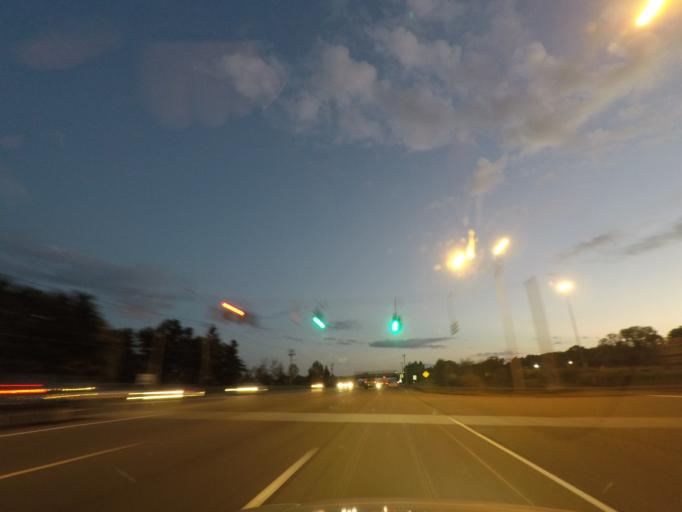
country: US
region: New York
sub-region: Orange County
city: Gardnertown
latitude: 41.5109
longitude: -74.0671
